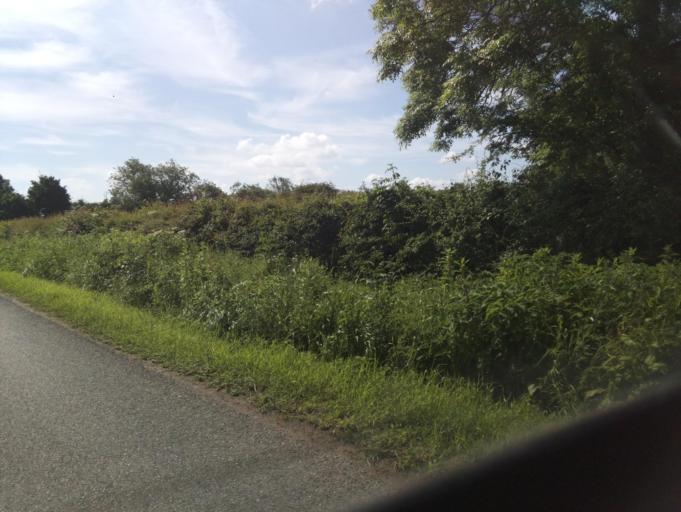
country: GB
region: England
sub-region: Lincolnshire
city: Skellingthorpe
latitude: 53.1587
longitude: -0.6355
